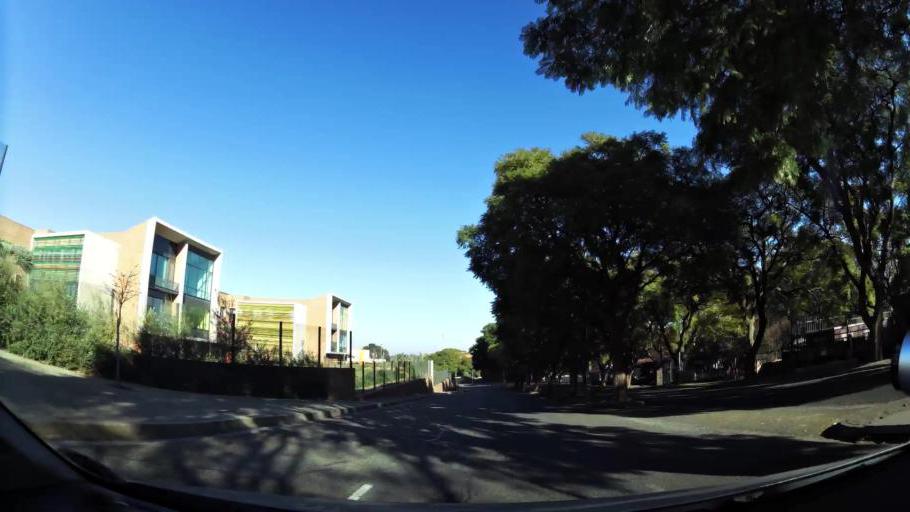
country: ZA
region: Gauteng
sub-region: City of Johannesburg Metropolitan Municipality
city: Johannesburg
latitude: -26.1787
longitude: 28.0389
